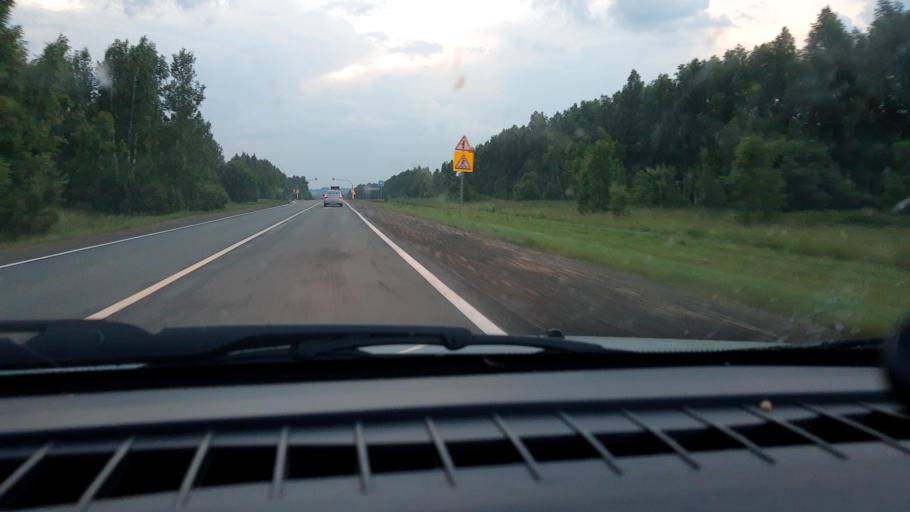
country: RU
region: Nizjnij Novgorod
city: Surovatikha
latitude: 55.7532
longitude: 43.9922
